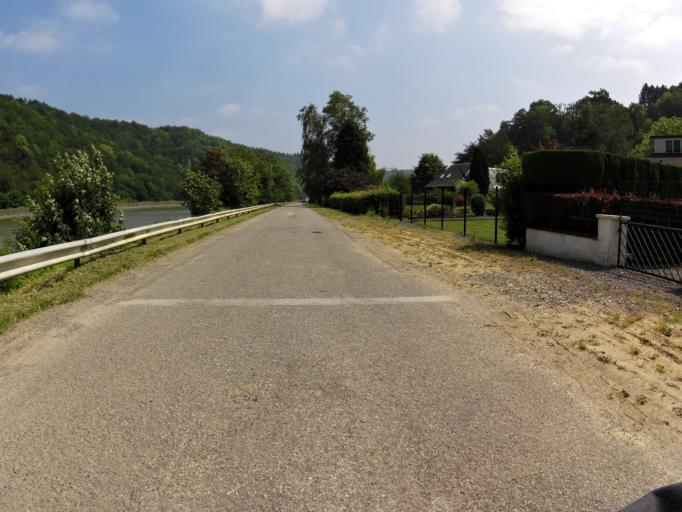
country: BE
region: Wallonia
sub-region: Province de Namur
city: Hastiere-Lavaux
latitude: 50.2140
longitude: 4.8413
